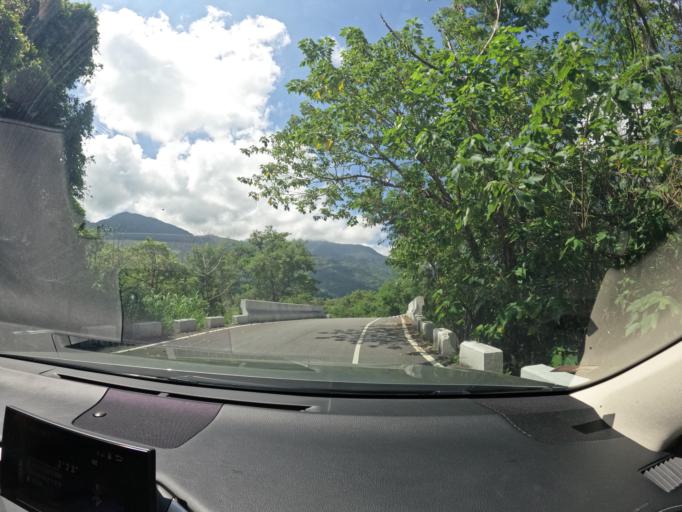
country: TW
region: Taiwan
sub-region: Hualien
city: Hualian
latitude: 23.6861
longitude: 121.4026
